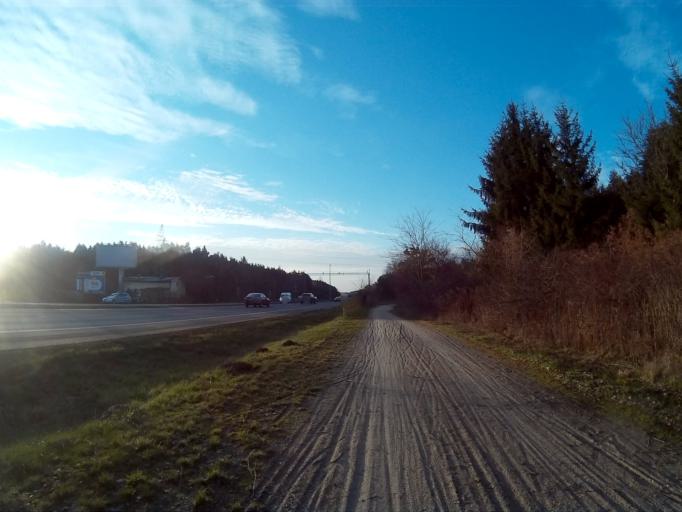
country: PL
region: Kujawsko-Pomorskie
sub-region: Powiat bydgoski
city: Osielsko
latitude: 53.1612
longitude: 18.0540
